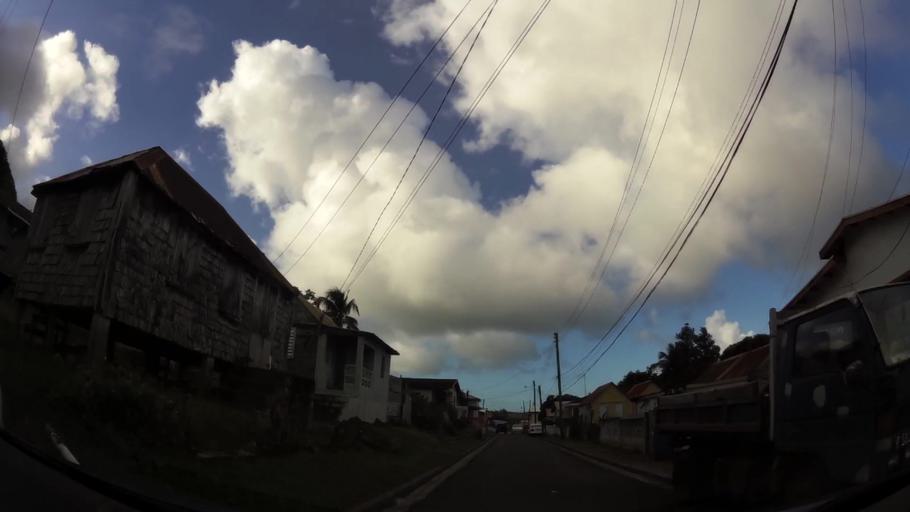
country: KN
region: Saint Mary Cayon
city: Cayon
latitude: 17.3511
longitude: -62.7334
